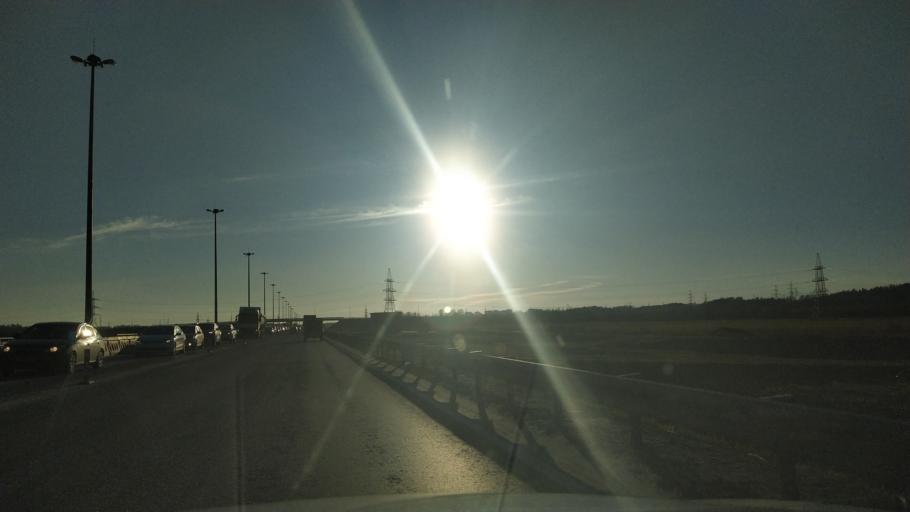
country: RU
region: Leningrad
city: Parnas
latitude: 60.0948
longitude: 30.3442
